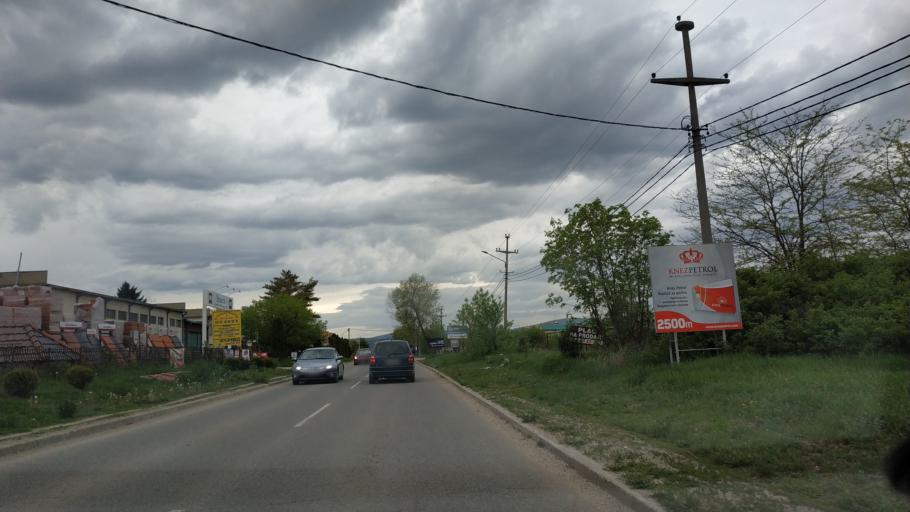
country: RS
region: Central Serbia
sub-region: Zajecarski Okrug
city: Soko Banja
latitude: 43.6516
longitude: 21.8507
